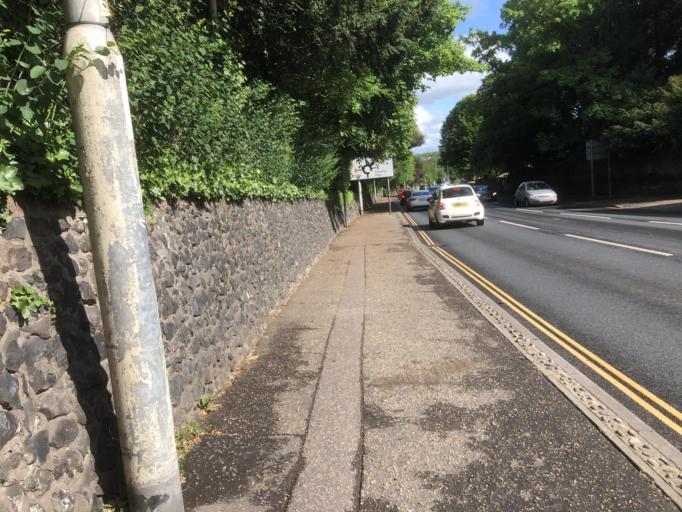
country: GB
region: England
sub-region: Norfolk
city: Thorpe Hamlet
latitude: 52.6171
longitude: 1.3088
